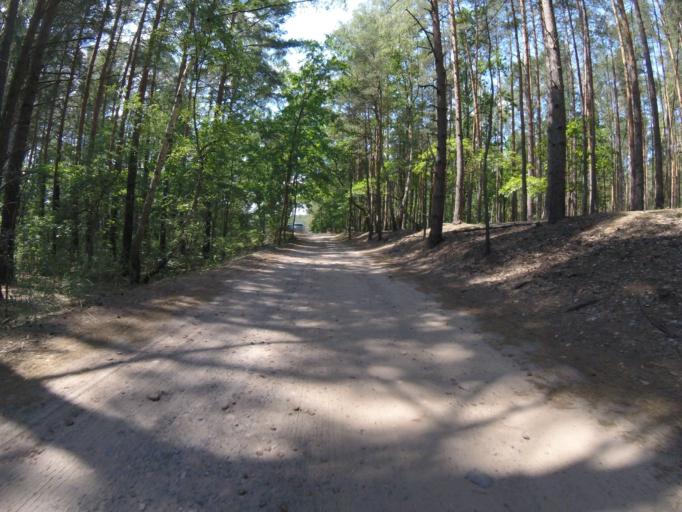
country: DE
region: Brandenburg
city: Bestensee
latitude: 52.2539
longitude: 13.6667
